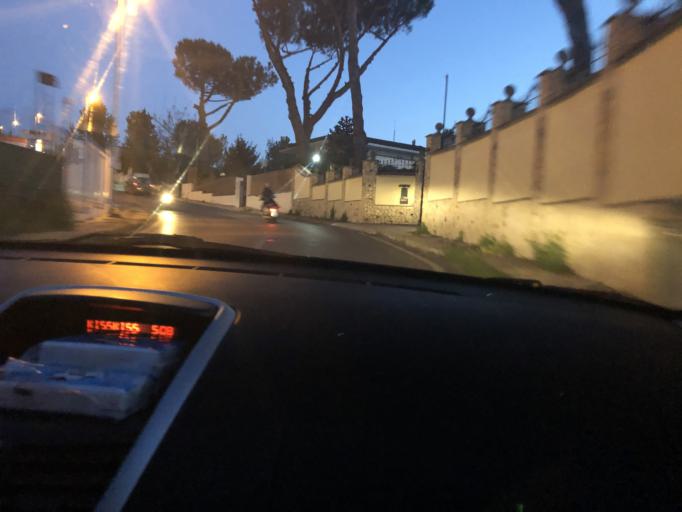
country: IT
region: Campania
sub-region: Provincia di Napoli
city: Marano di Napoli
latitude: 40.8907
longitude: 14.1791
